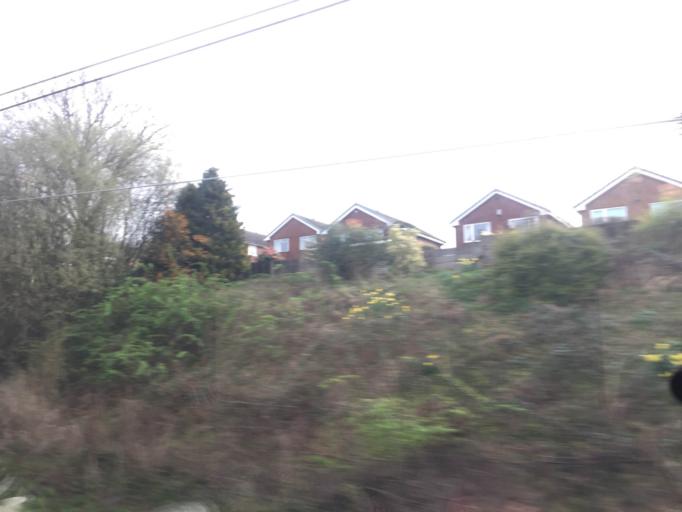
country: GB
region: England
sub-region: Borough of Wigan
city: Ince-in-Makerfield
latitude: 53.5671
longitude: -2.6402
